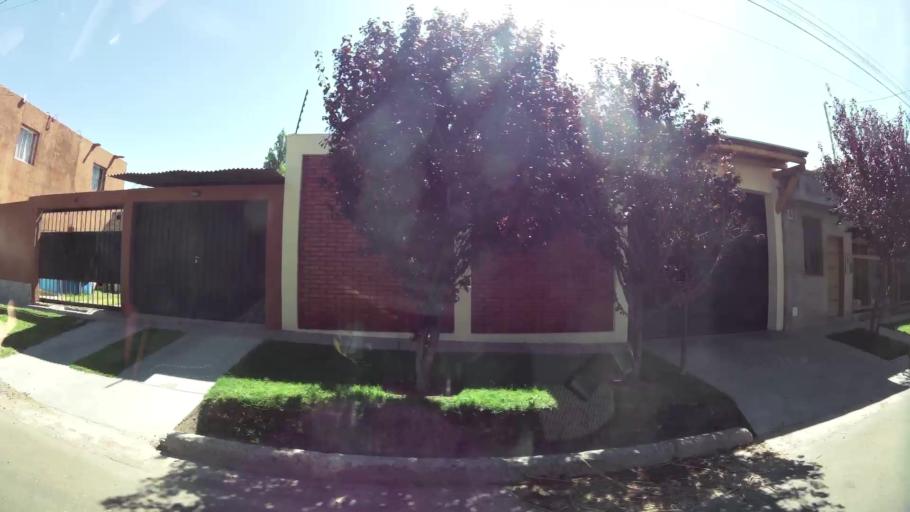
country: AR
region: Mendoza
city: Villa Nueva
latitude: -32.9012
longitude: -68.7786
